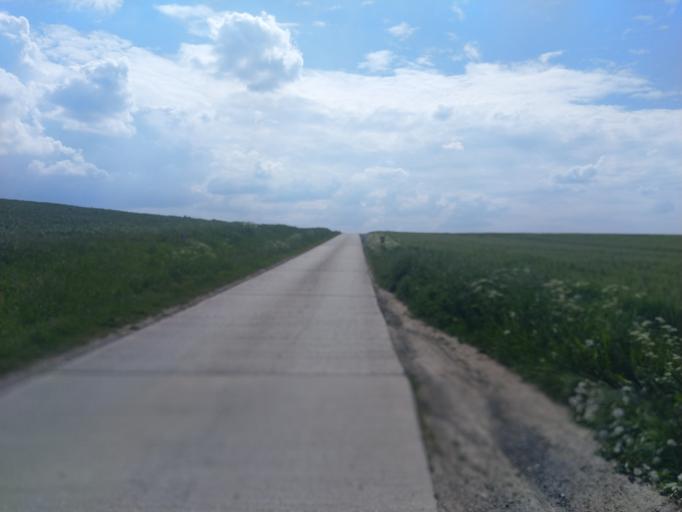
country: BE
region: Wallonia
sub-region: Province du Hainaut
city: Chasse Royale
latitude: 50.4250
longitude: 3.9801
